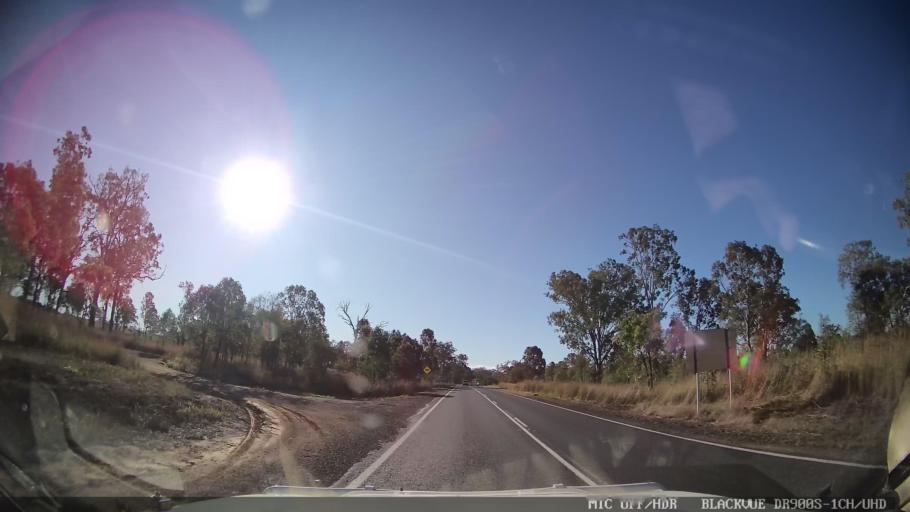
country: AU
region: Queensland
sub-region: Bundaberg
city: Sharon
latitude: -24.8254
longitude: 151.7067
